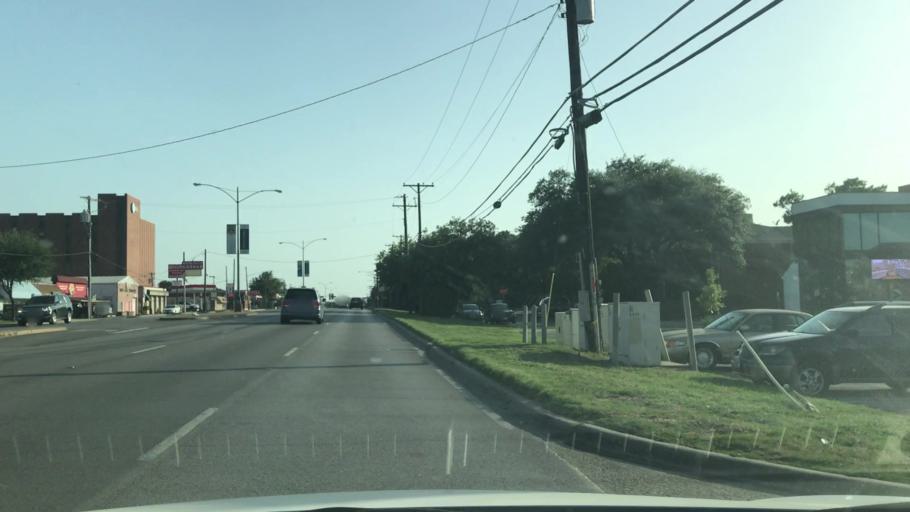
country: US
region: Texas
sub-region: Dallas County
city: Highland Park
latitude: 32.8275
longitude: -96.7098
